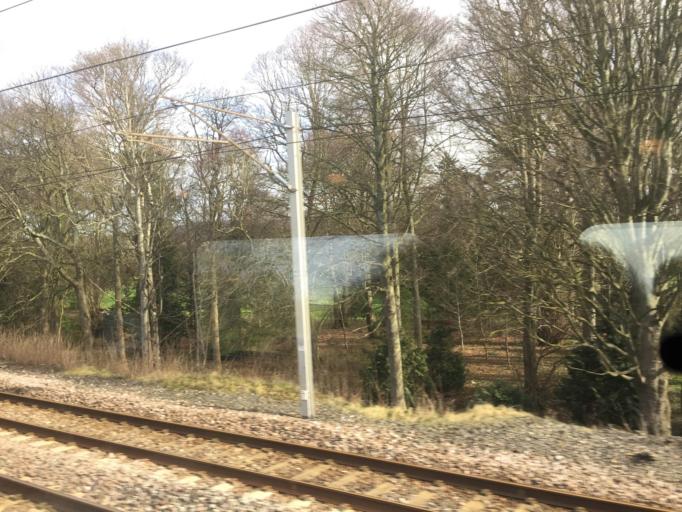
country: GB
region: England
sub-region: Cumbria
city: Penrith
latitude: 54.6497
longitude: -2.7665
